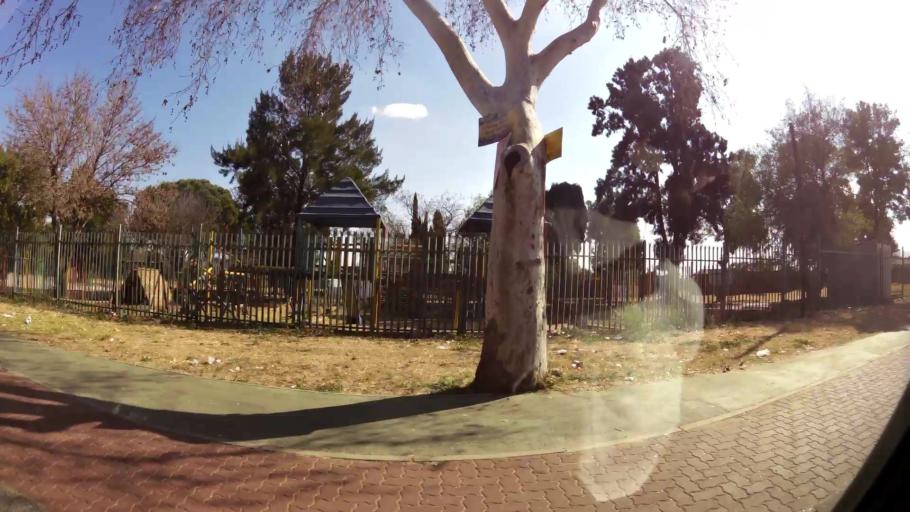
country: ZA
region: Gauteng
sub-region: City of Johannesburg Metropolitan Municipality
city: Soweto
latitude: -26.2459
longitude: 27.8933
